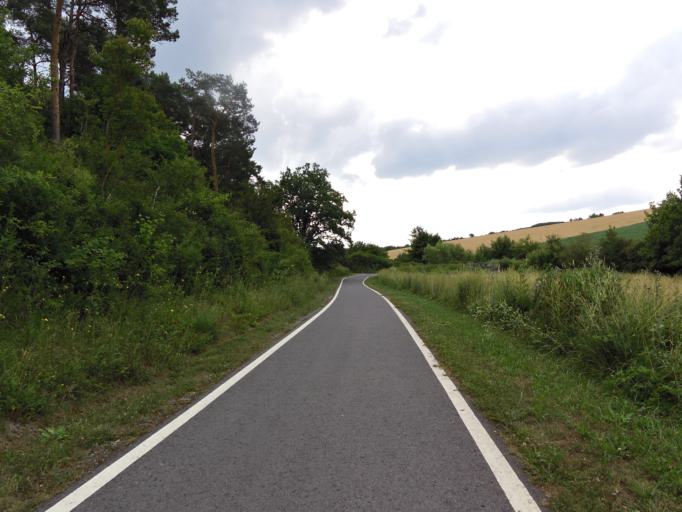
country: DE
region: Bavaria
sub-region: Regierungsbezirk Unterfranken
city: Reichenberg
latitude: 49.7295
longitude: 9.9514
